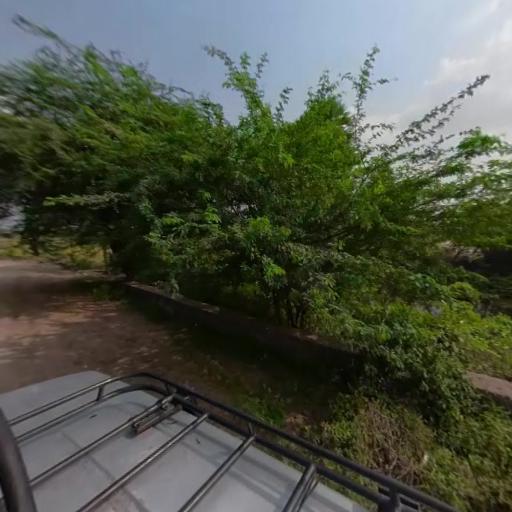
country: IN
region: Telangana
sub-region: Nalgonda
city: Suriapet
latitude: 17.2042
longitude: 79.4854
